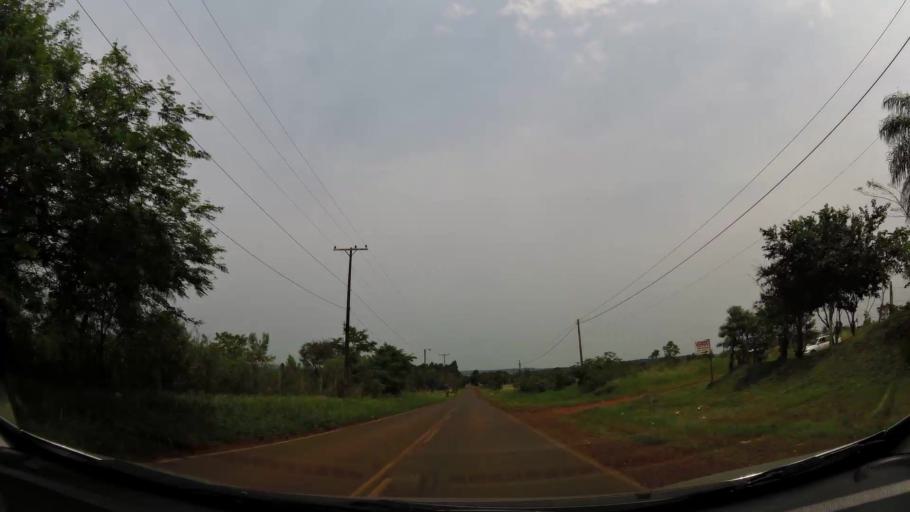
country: AR
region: Misiones
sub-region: Departamento de Iguazu
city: Puerto Iguazu
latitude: -25.5807
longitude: -54.6030
